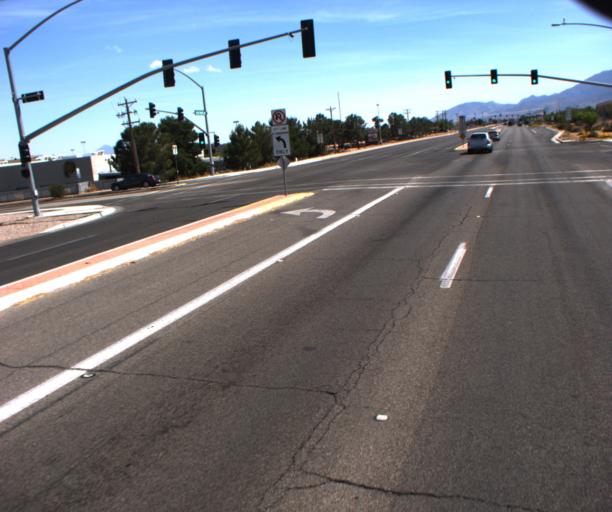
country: US
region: Arizona
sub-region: Cochise County
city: Sierra Vista
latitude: 31.5623
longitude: -110.2574
